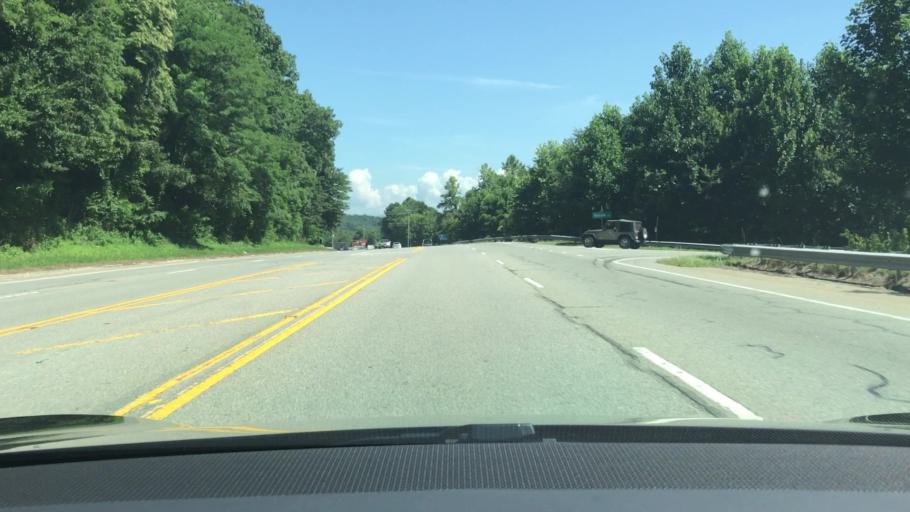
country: US
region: North Carolina
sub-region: Macon County
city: Franklin
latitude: 35.0896
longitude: -83.3834
